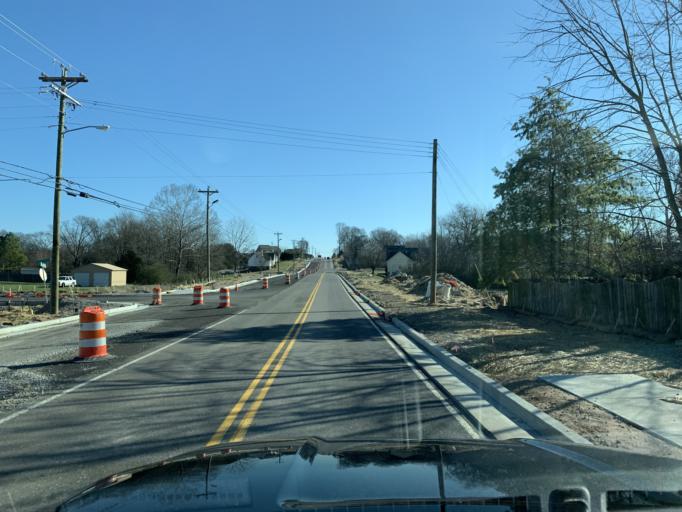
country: US
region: Tennessee
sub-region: Maury County
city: Spring Hill
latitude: 35.7526
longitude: -86.8947
